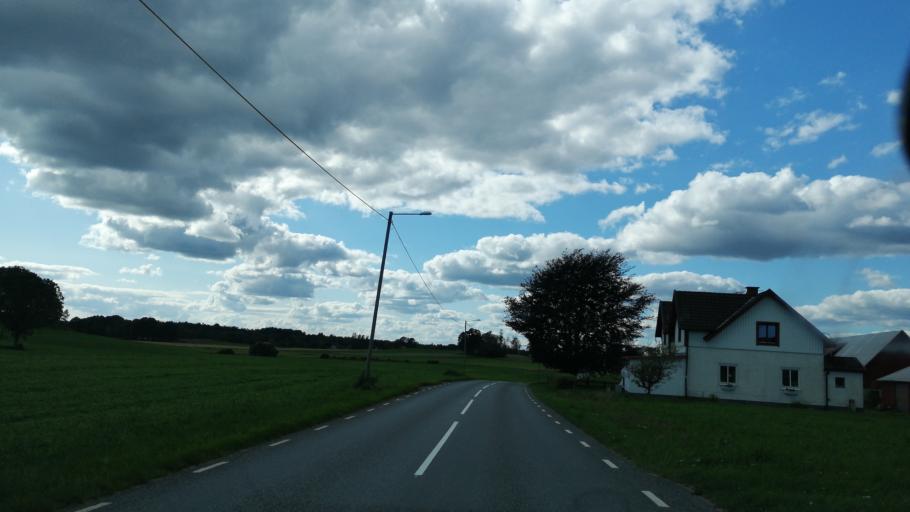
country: SE
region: Joenkoeping
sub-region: Gislaveds Kommun
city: Reftele
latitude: 57.1657
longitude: 13.6132
